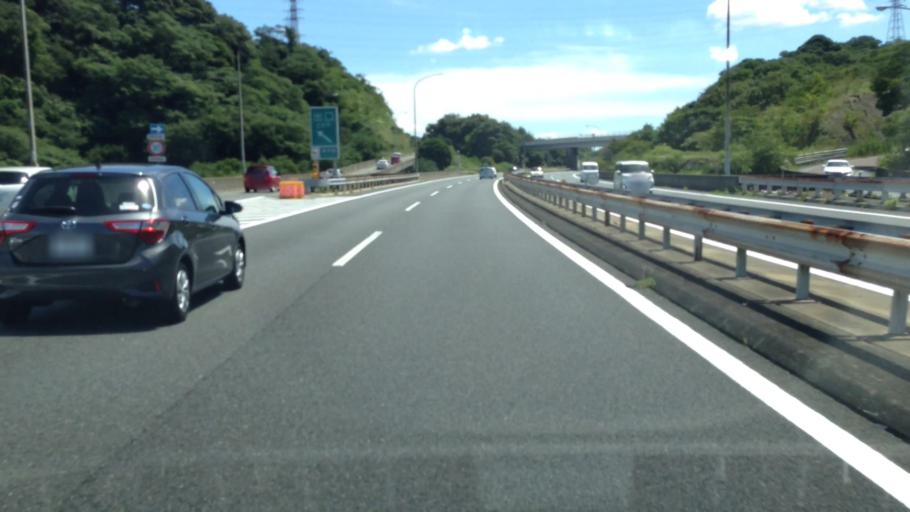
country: JP
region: Kanagawa
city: Yokosuka
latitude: 35.2792
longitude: 139.6322
